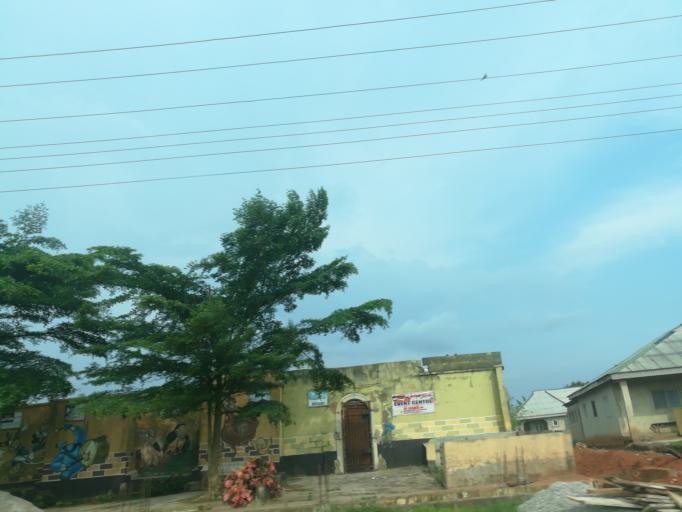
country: NG
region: Lagos
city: Ikorodu
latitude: 6.6524
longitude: 3.6697
